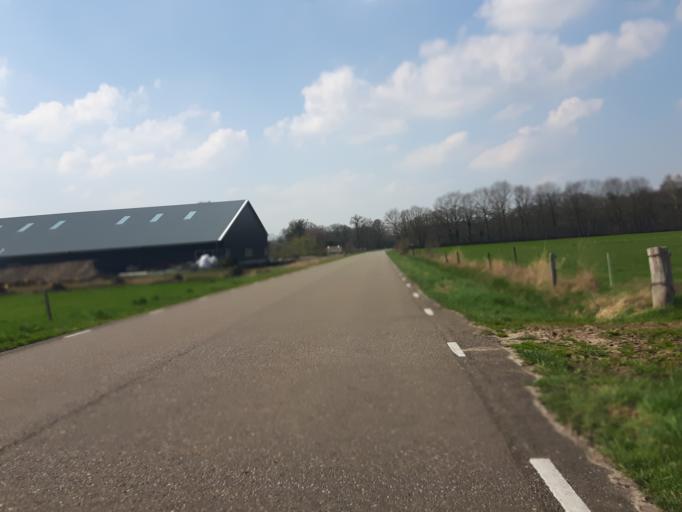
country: NL
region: Overijssel
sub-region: Gemeente Haaksbergen
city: Haaksbergen
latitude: 52.1875
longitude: 6.8093
